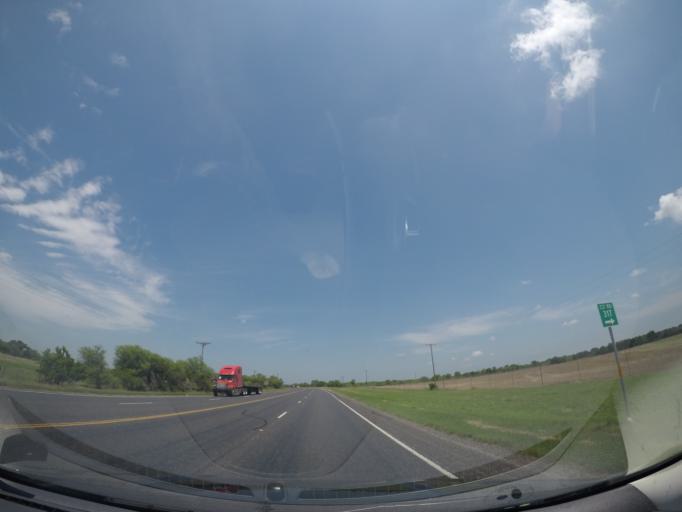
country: US
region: Texas
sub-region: Uvalde County
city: Sabinal
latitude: 29.3141
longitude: -99.4446
